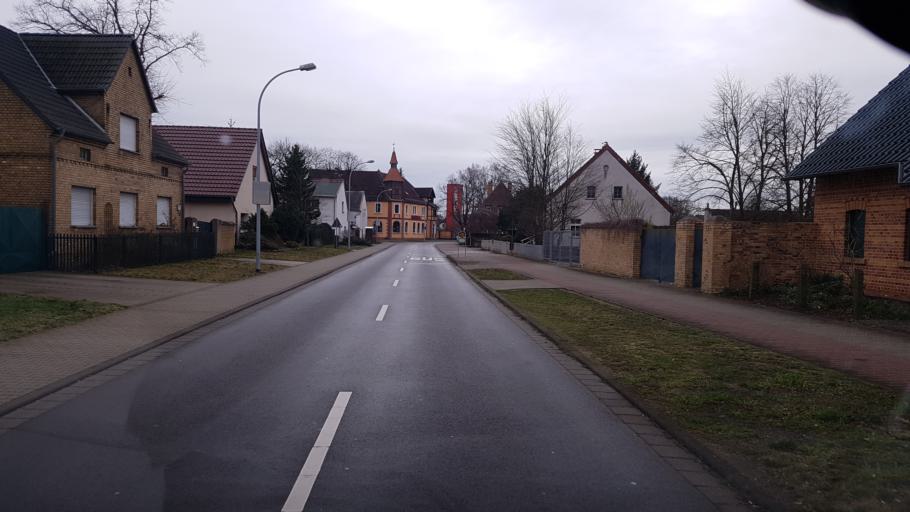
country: DE
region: Brandenburg
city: Ruhland
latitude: 51.4721
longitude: 13.8901
